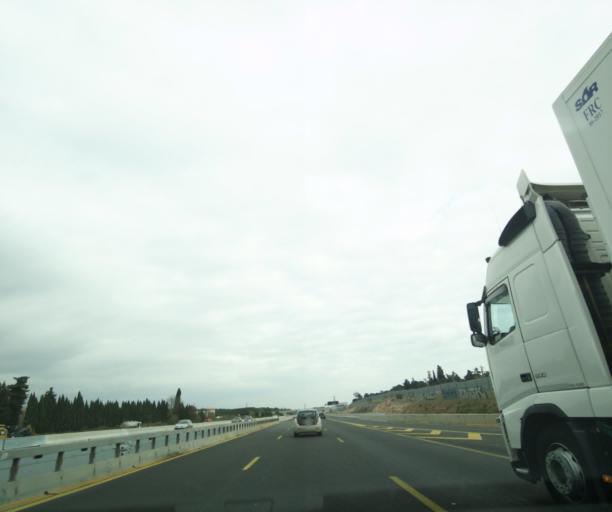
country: FR
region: Languedoc-Roussillon
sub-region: Departement de l'Herault
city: Saint-Jean-de-Vedas
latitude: 43.5672
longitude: 3.8432
